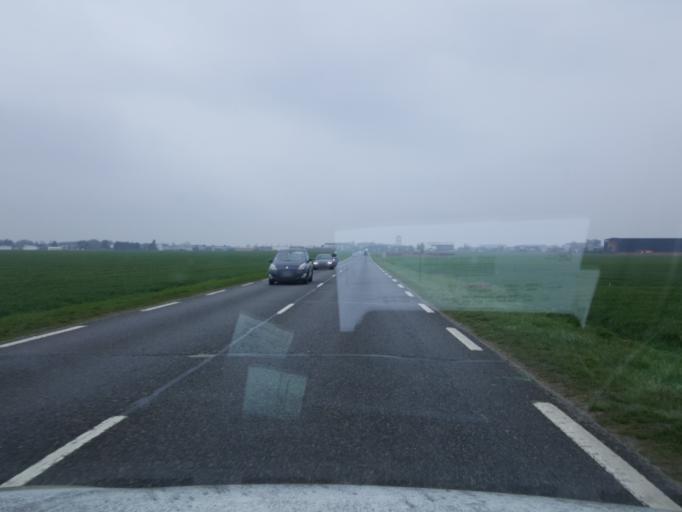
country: FR
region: Centre
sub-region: Departement d'Eure-et-Loir
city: Vernouillet
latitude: 48.7026
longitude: 1.3734
